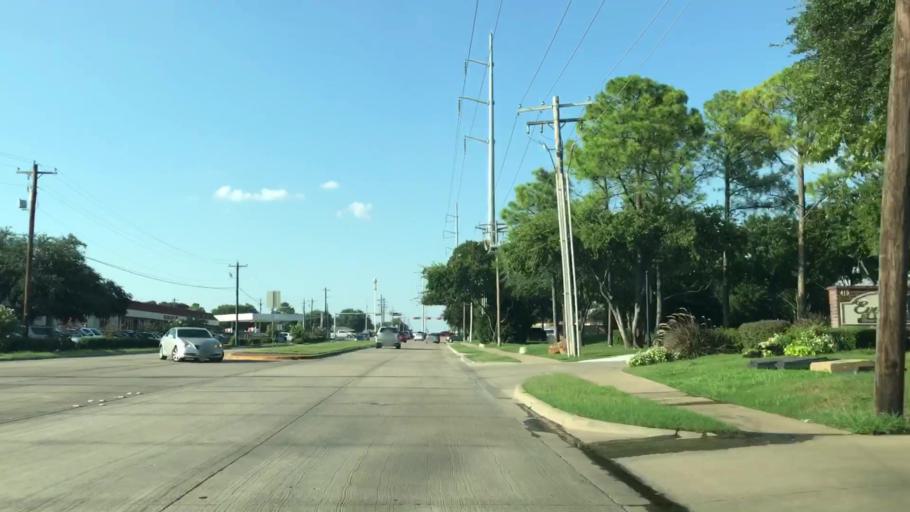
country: US
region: Texas
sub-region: Denton County
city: Lewisville
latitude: 33.0403
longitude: -97.0360
